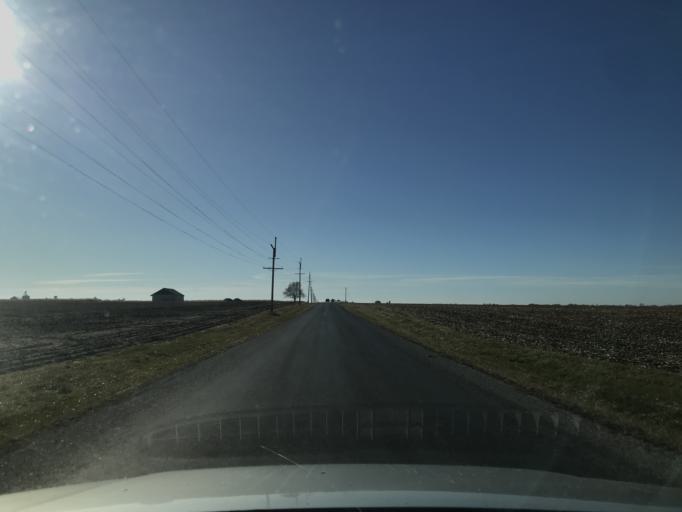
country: US
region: Illinois
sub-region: Hancock County
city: Carthage
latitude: 40.4861
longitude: -91.1780
